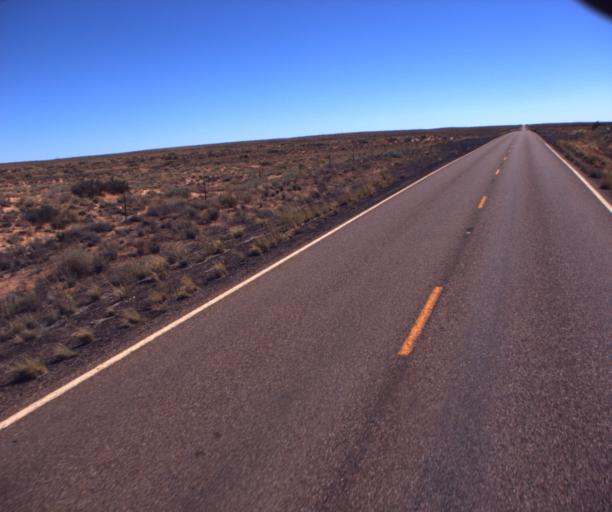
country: US
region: Arizona
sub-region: Navajo County
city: Holbrook
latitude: 35.0311
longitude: -110.0907
